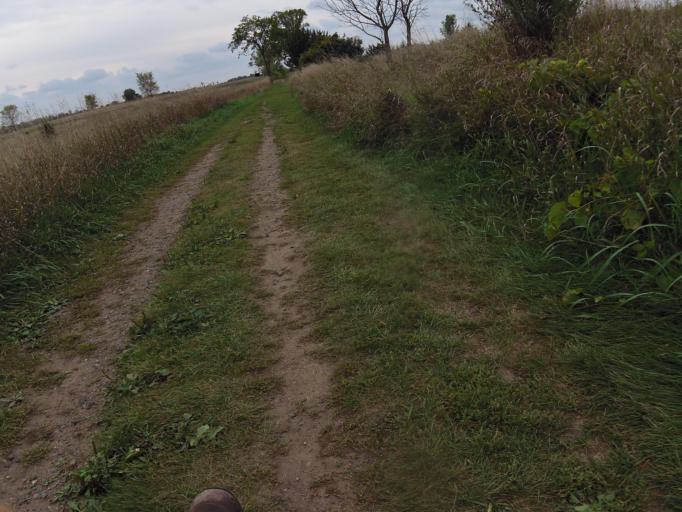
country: US
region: Minnesota
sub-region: Washington County
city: Afton
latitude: 44.8735
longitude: -92.7918
